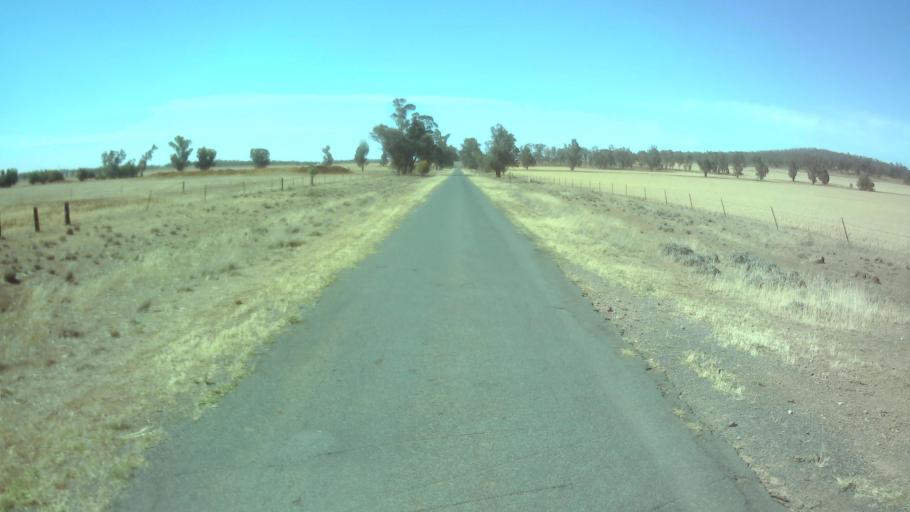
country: AU
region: New South Wales
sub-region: Forbes
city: Forbes
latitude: -33.7388
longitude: 147.7411
